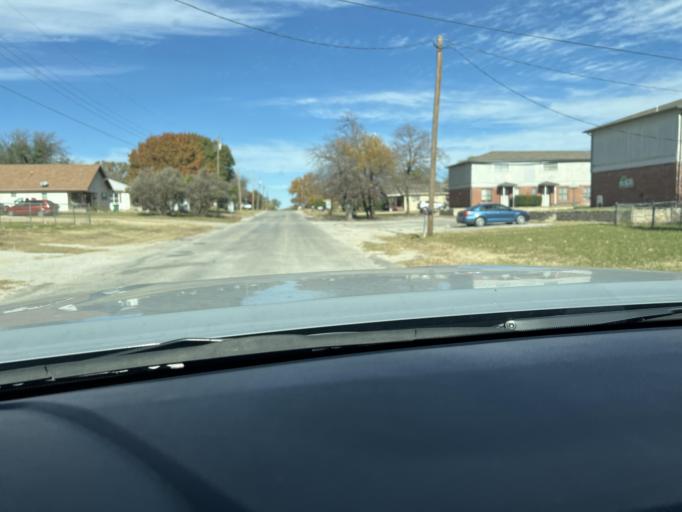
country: US
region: Texas
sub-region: Eastland County
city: Eastland
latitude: 32.3956
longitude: -98.8307
